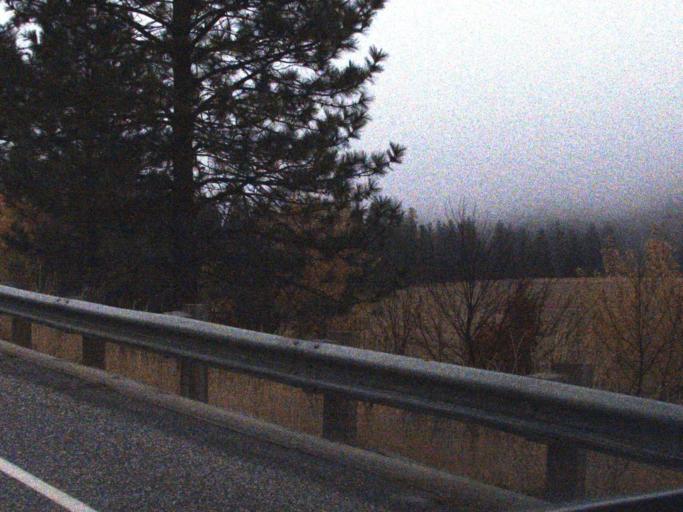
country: US
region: Washington
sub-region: Stevens County
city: Kettle Falls
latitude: 48.6927
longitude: -118.1250
